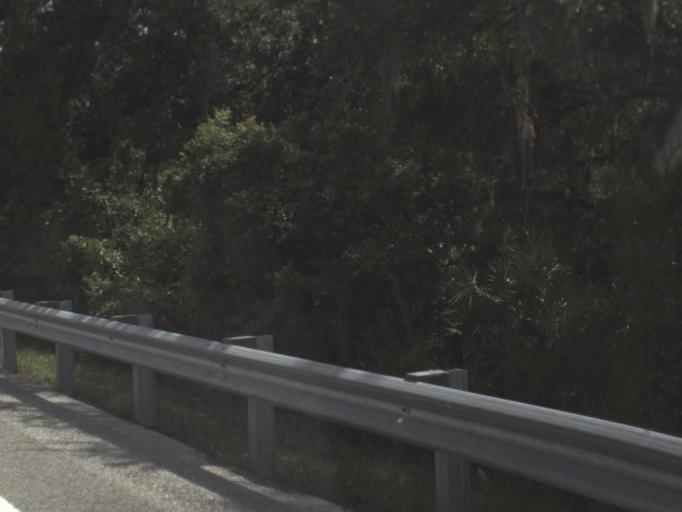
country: US
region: Florida
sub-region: Sarasota County
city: Lake Sarasota
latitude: 27.2292
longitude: -82.3051
